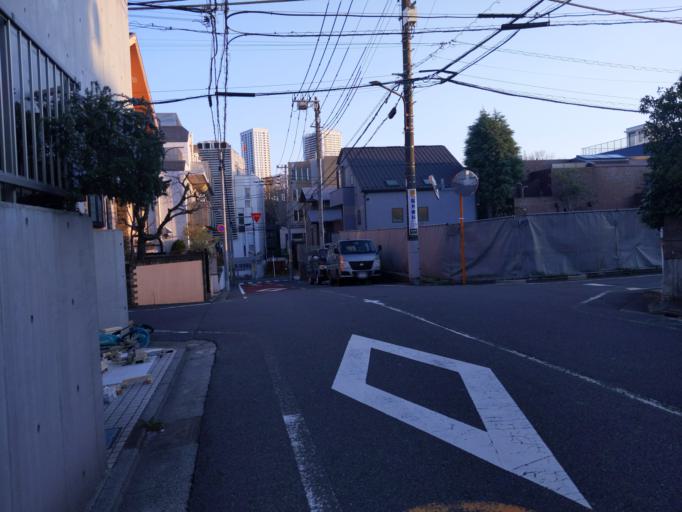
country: JP
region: Tokyo
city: Tokyo
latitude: 35.6272
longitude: 139.7030
